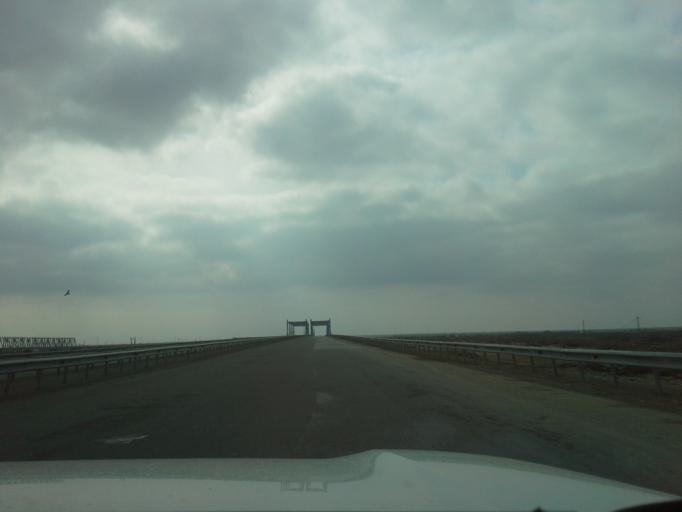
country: TM
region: Ahal
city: Tejen
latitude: 37.2355
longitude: 60.1588
